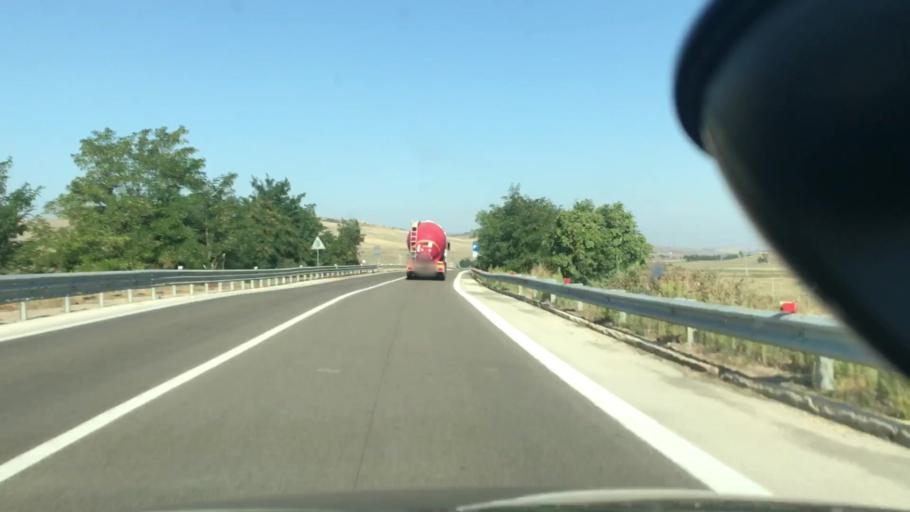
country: IT
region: Basilicate
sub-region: Provincia di Matera
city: Irsina
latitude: 40.7889
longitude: 16.2872
